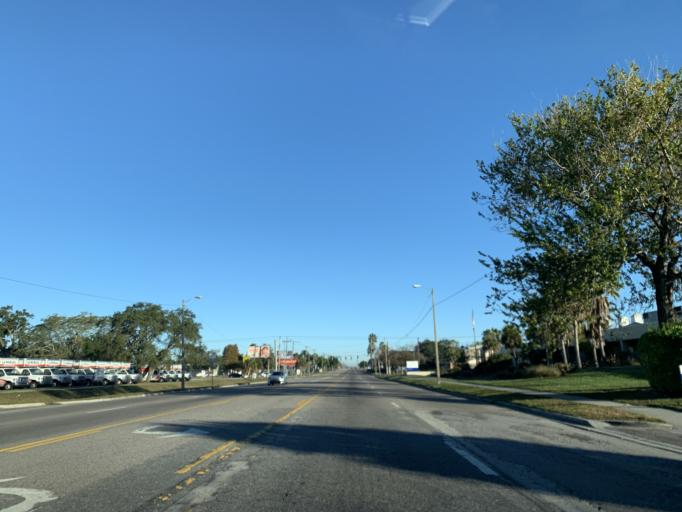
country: US
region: Florida
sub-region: Hillsborough County
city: University
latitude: 28.0421
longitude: -82.4262
